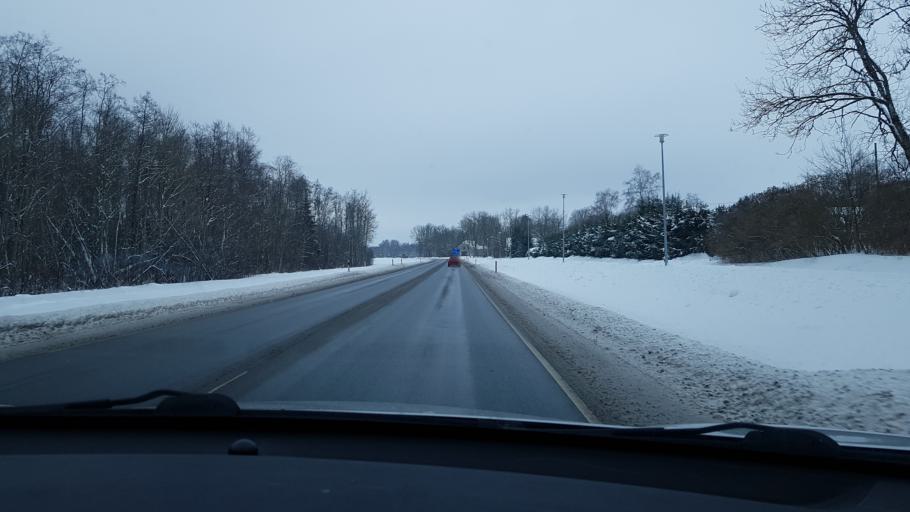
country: EE
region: Jaervamaa
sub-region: Tueri vald
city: Tueri
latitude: 58.8534
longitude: 25.4827
